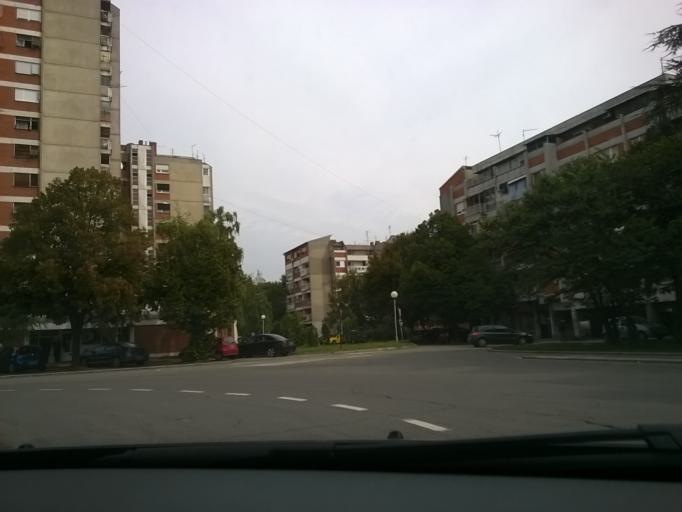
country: RS
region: Autonomna Pokrajina Vojvodina
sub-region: Juznobanatski Okrug
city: Pancevo
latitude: 44.8793
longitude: 20.6542
